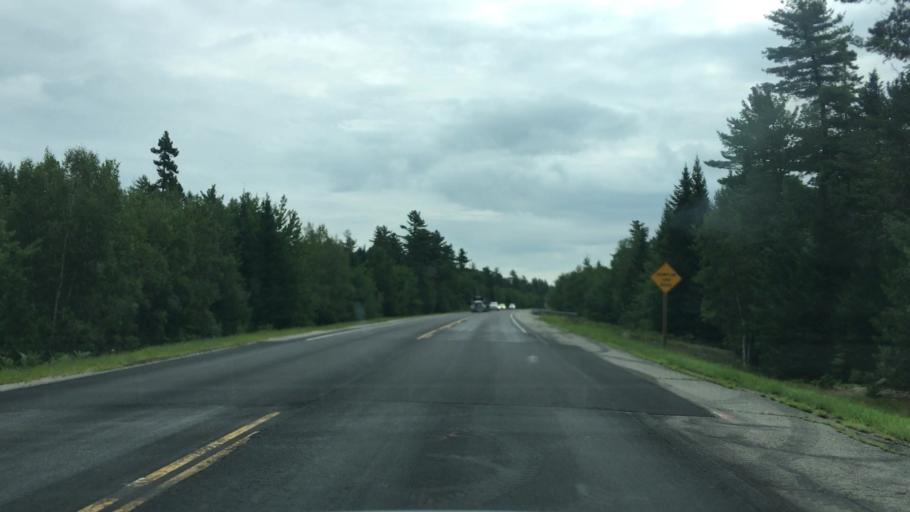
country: US
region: Maine
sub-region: Washington County
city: Addison
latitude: 44.9071
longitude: -67.8309
